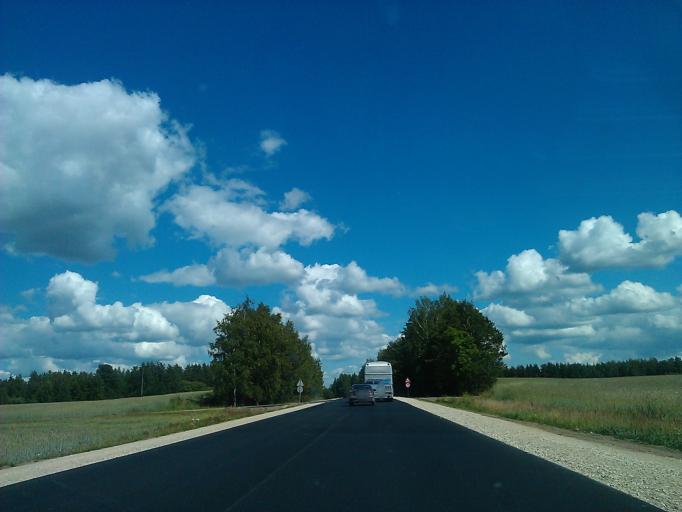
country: LV
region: Vilanu
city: Vilani
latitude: 56.5606
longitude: 27.0333
